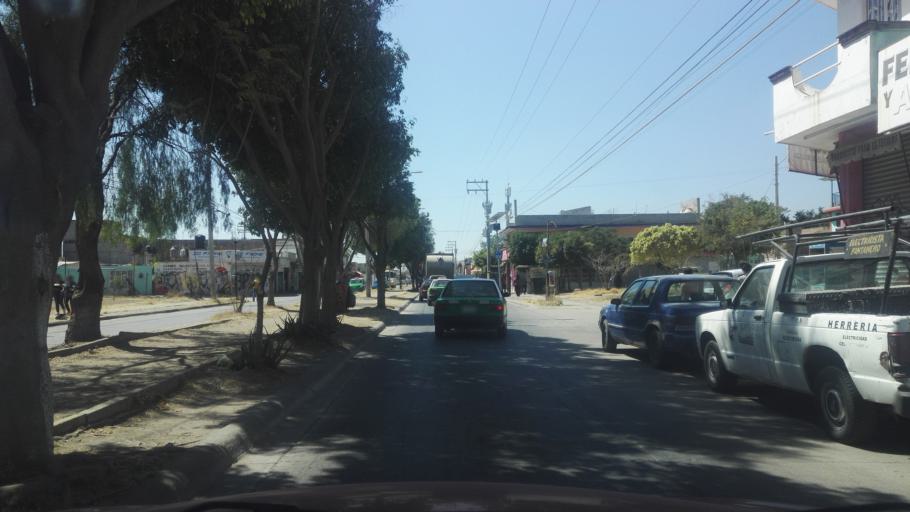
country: MX
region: Guanajuato
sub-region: Leon
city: Fraccionamiento Paraiso Real
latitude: 21.0979
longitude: -101.5889
